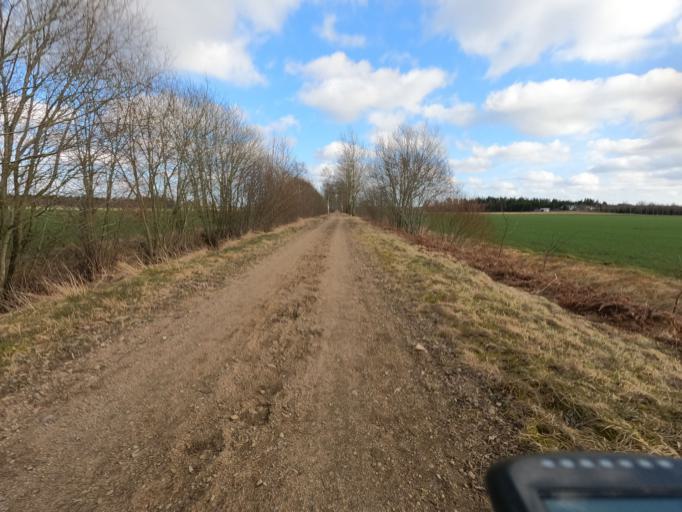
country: SE
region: Kronoberg
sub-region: Alvesta Kommun
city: Vislanda
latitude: 56.7327
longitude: 14.5535
